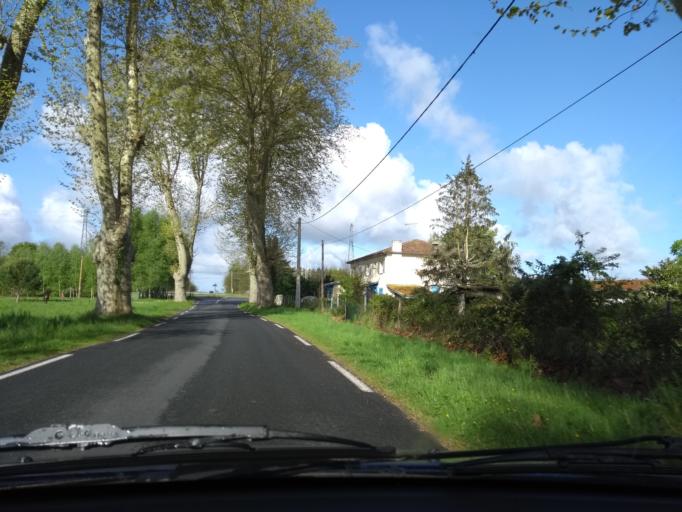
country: FR
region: Aquitaine
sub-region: Departement de la Gironde
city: Mios
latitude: 44.5495
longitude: -0.9899
